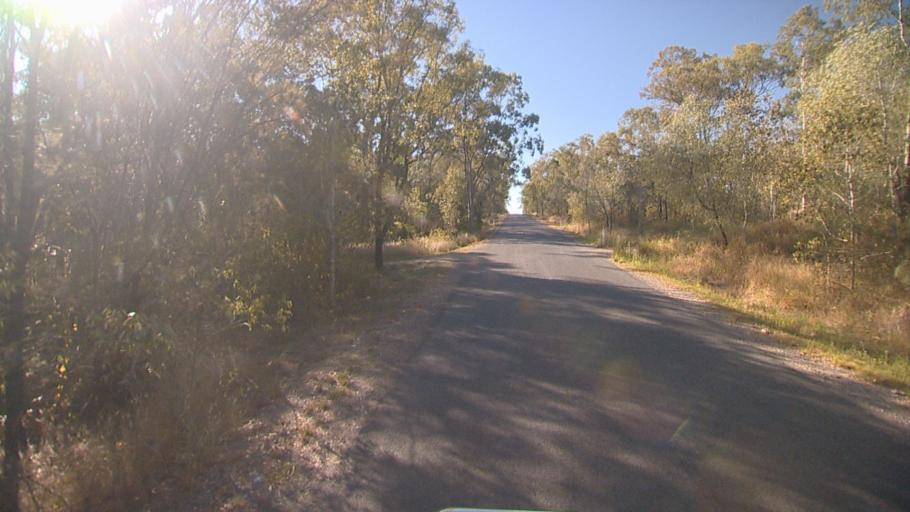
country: AU
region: Queensland
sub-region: Logan
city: North Maclean
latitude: -27.8014
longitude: 153.0252
